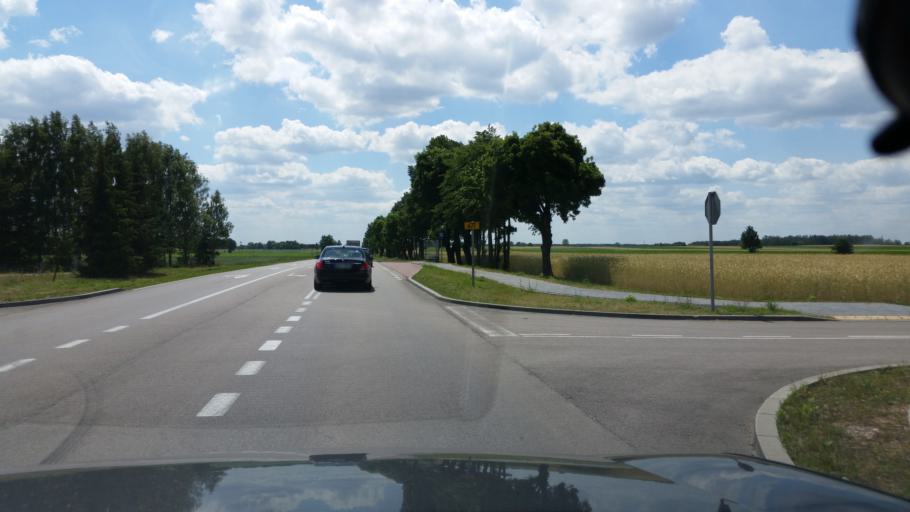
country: PL
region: Masovian Voivodeship
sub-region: Powiat ostrowski
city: Ostrow Mazowiecka
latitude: 52.8920
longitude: 21.8673
